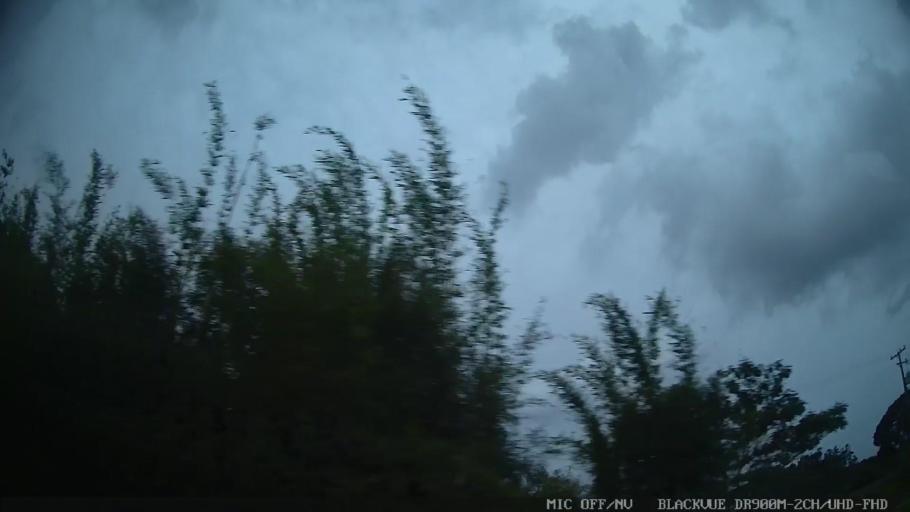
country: BR
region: Sao Paulo
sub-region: Braganca Paulista
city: Braganca Paulista
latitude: -22.9444
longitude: -46.6294
